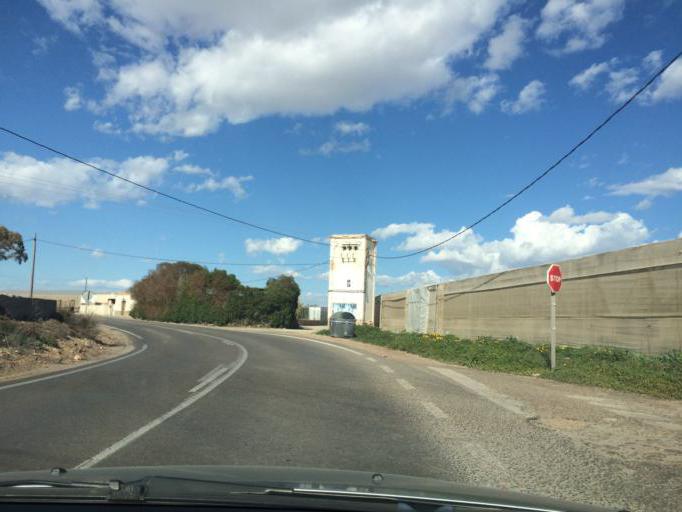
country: ES
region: Andalusia
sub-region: Provincia de Almeria
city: Retamar
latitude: 36.7813
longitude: -2.2256
